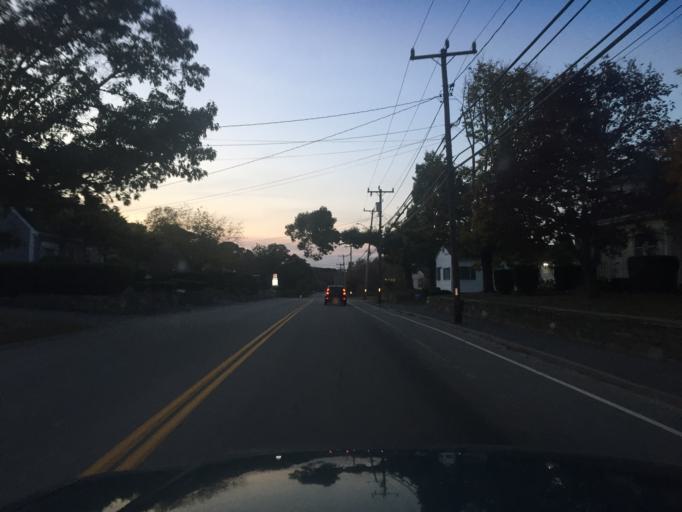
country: US
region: Massachusetts
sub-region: Plymouth County
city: Onset
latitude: 41.7518
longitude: -70.6714
